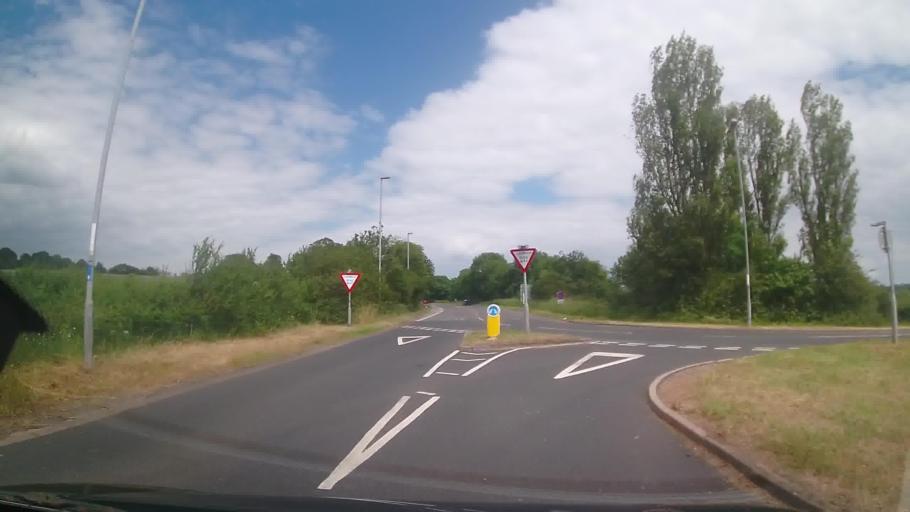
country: GB
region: Wales
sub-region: Monmouthshire
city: Llanarth
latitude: 51.7694
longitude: -2.8400
